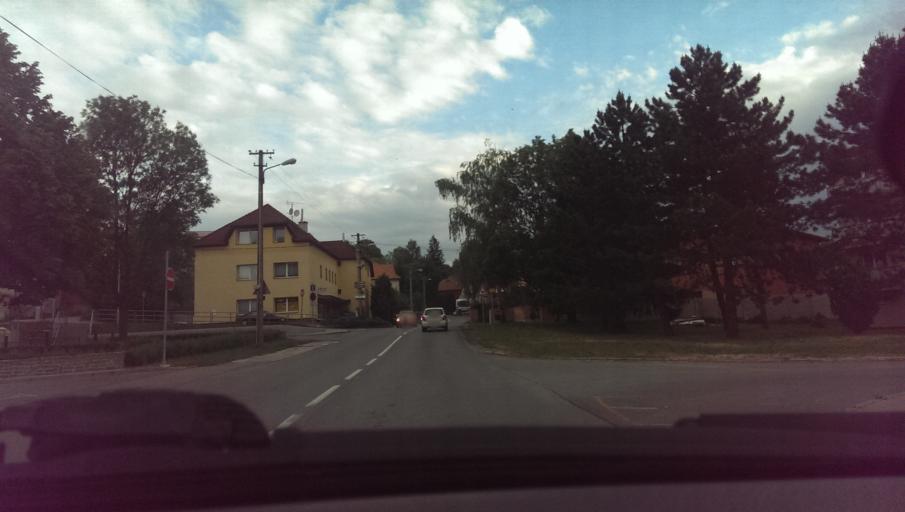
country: CZ
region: Zlin
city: Bilovice
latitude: 49.1000
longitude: 17.5478
